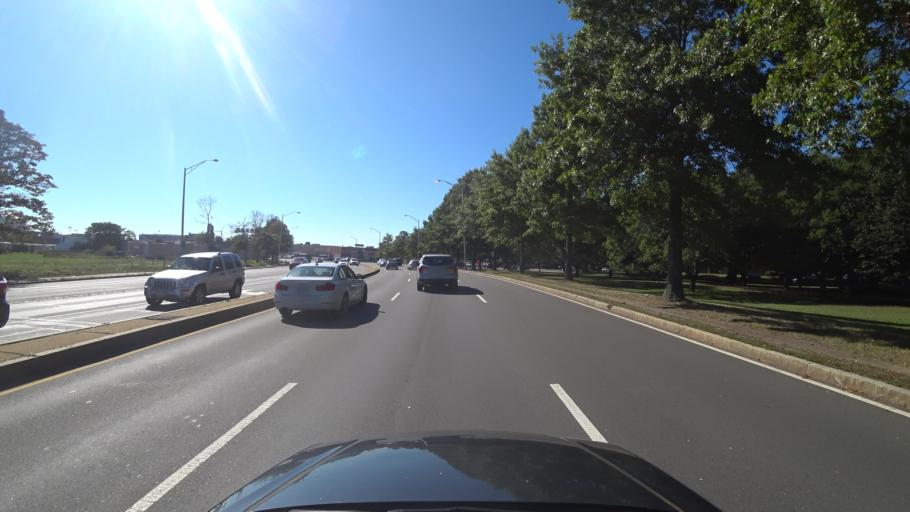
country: US
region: Massachusetts
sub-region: Essex County
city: Lynn
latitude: 42.4603
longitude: -70.9456
